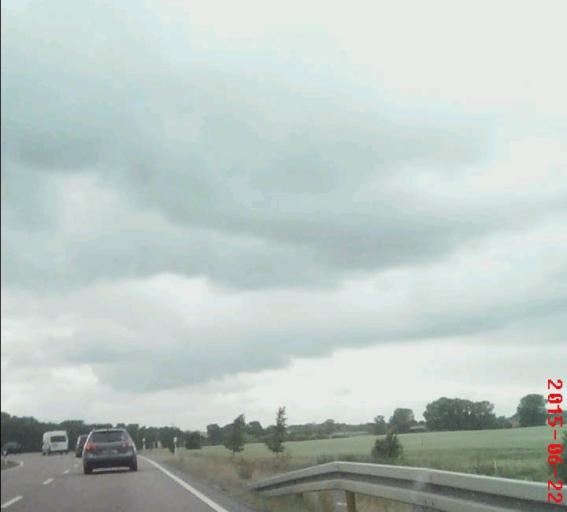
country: DE
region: Saxony-Anhalt
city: Angersdorf
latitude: 51.4637
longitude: 11.8903
